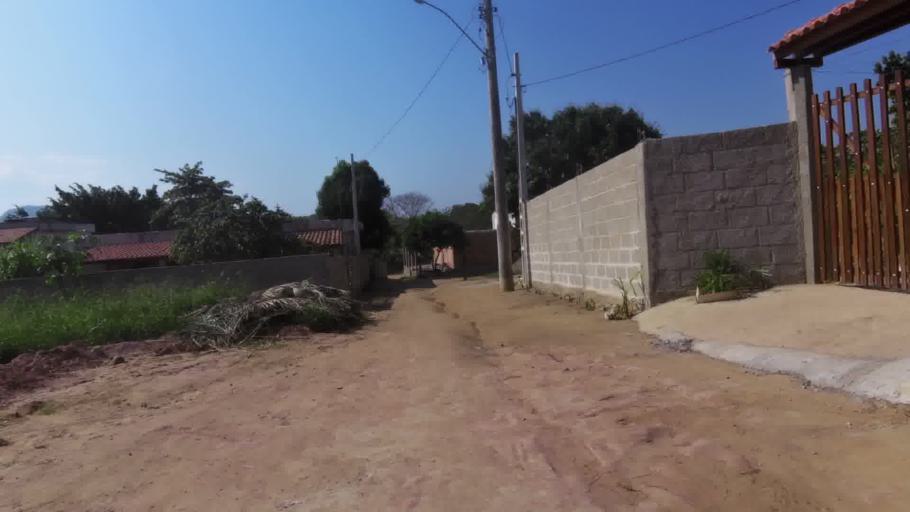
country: BR
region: Espirito Santo
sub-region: Piuma
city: Piuma
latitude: -20.8124
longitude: -40.7368
